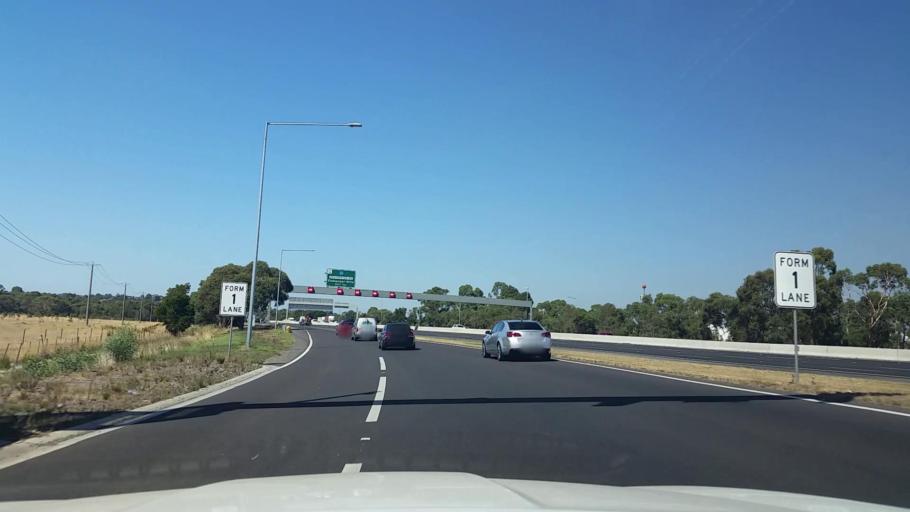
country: AU
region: Victoria
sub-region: Greater Dandenong
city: Dandenong North
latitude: -37.9602
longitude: 145.2267
